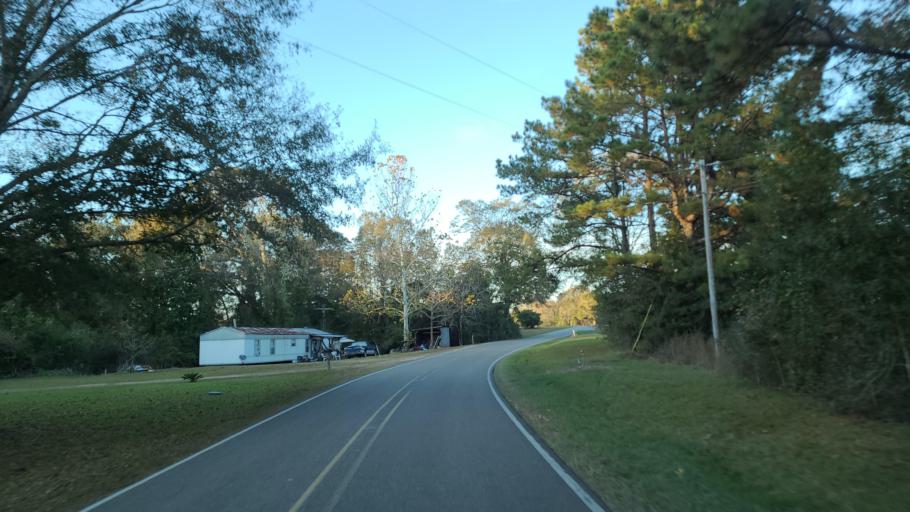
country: US
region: Mississippi
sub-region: Stone County
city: Wiggins
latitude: 30.9907
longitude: -89.2599
